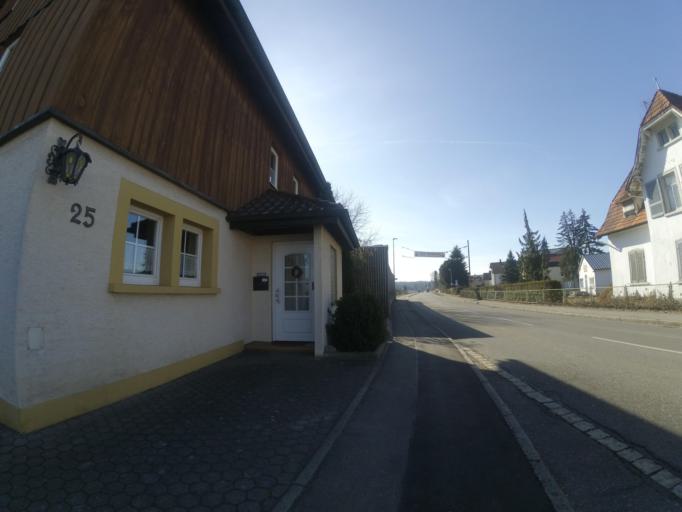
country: DE
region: Baden-Wuerttemberg
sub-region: Tuebingen Region
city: Baindt
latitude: 47.8704
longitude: 9.6382
